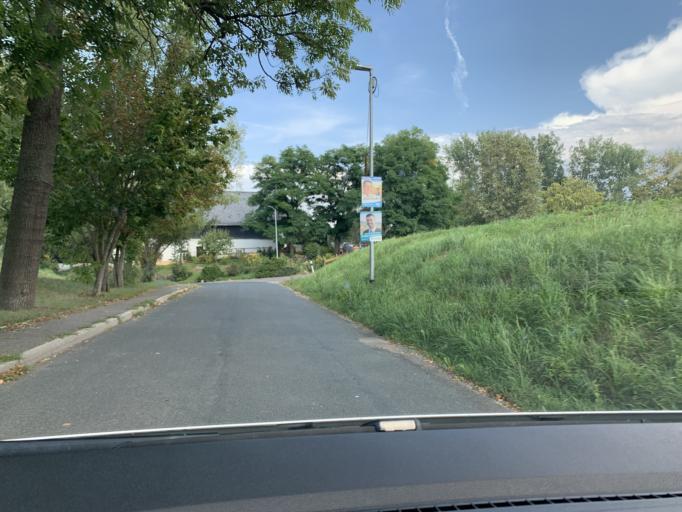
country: DE
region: Saxony
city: Frankenberg
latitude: 50.9197
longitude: 13.0685
